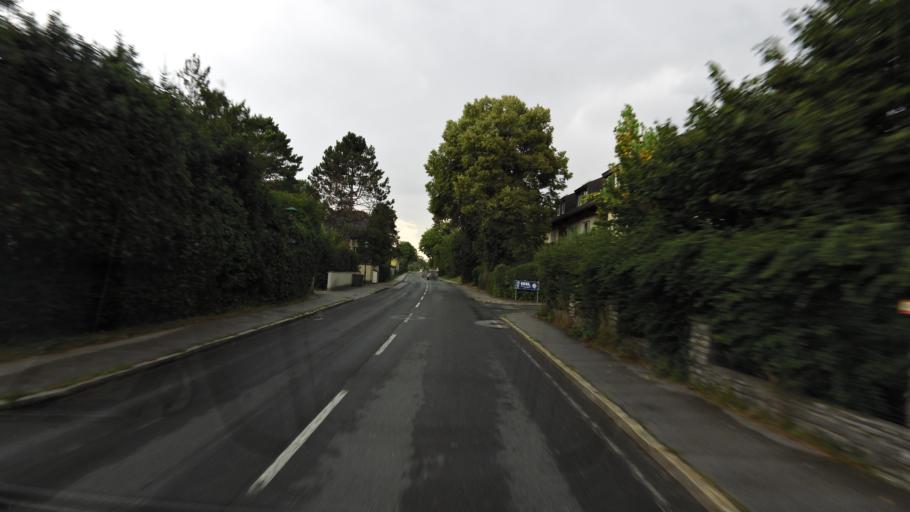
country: AT
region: Salzburg
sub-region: Politischer Bezirk Salzburg-Umgebung
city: Anif
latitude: 47.7528
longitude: 13.0647
